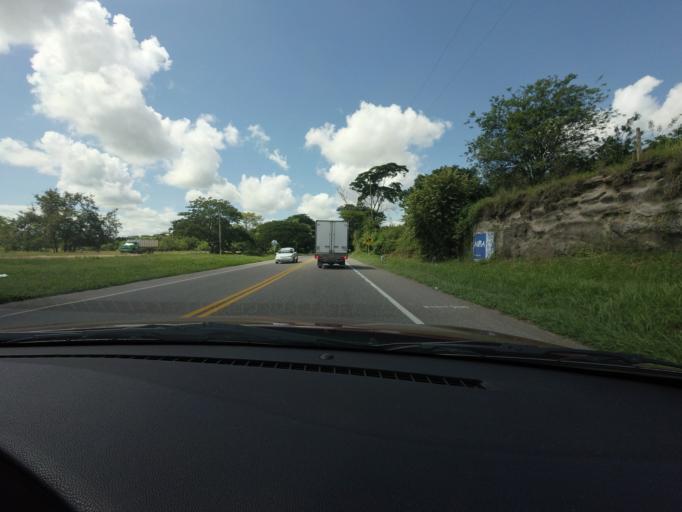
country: CO
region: Tolima
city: Saldana
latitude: 3.9400
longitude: -75.0152
